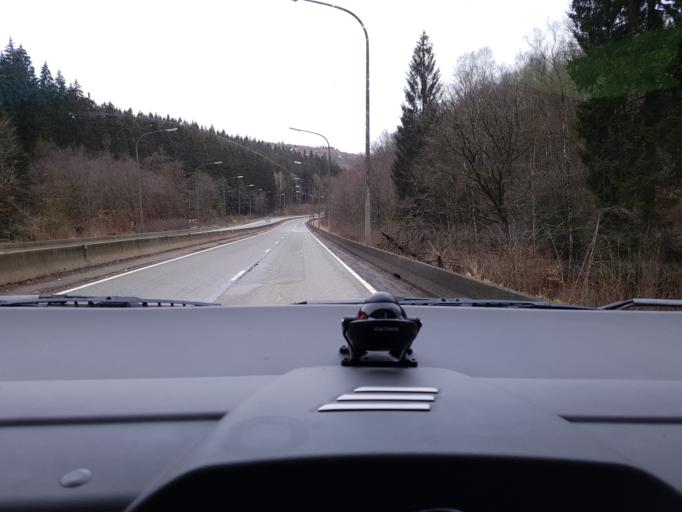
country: BE
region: Wallonia
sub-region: Province du Luxembourg
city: Tenneville
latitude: 50.1280
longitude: 5.4554
